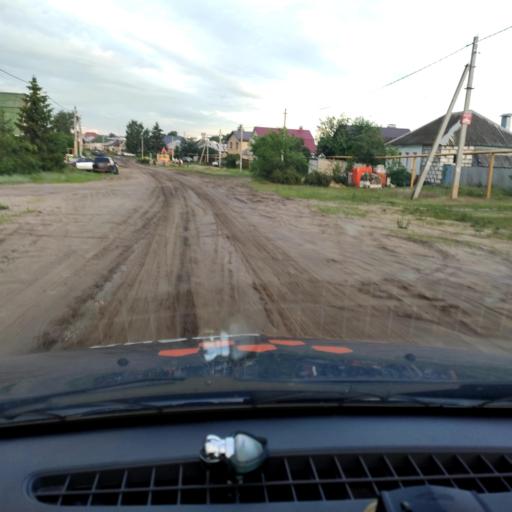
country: RU
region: Voronezj
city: Somovo
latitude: 51.7537
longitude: 39.3237
